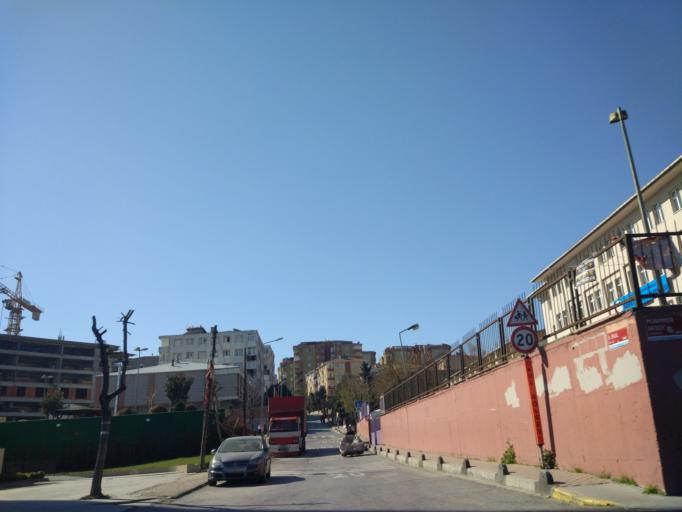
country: TR
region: Istanbul
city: Mahmutbey
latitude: 41.0227
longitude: 28.8059
